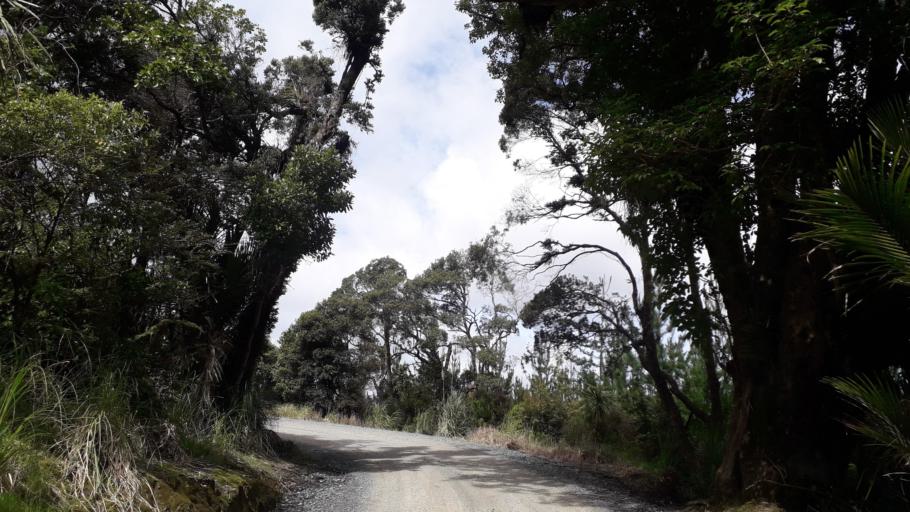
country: NZ
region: Northland
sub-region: Far North District
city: Kaitaia
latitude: -35.1925
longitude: 173.2848
